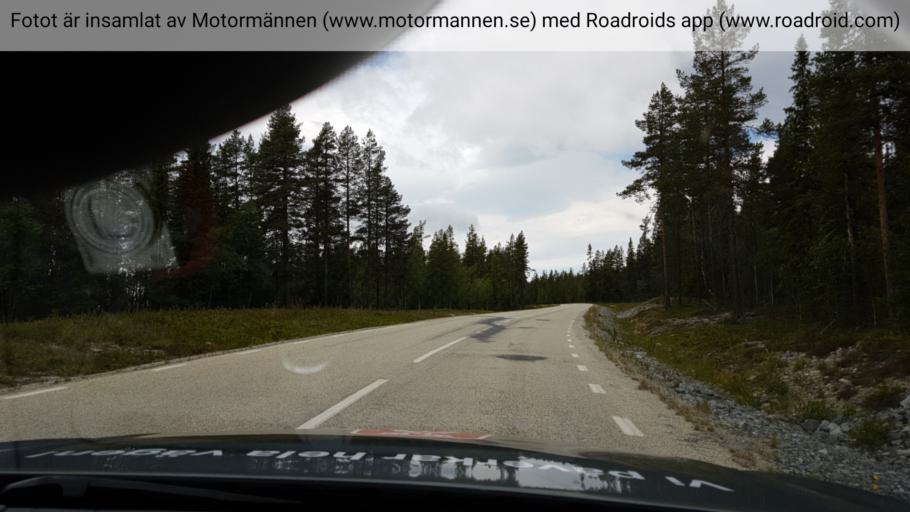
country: SE
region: Jaemtland
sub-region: Are Kommun
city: Jarpen
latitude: 62.8389
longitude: 13.2584
